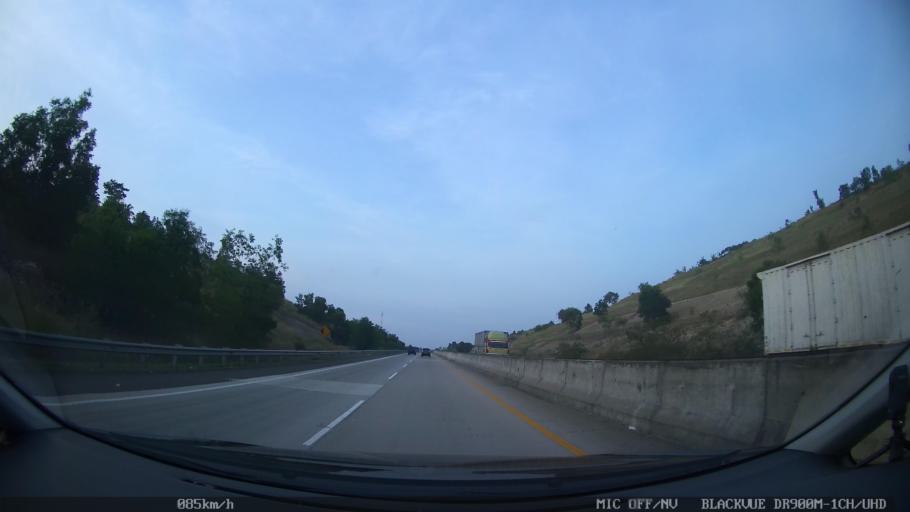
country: ID
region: Lampung
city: Penengahan
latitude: -5.8274
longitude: 105.7332
